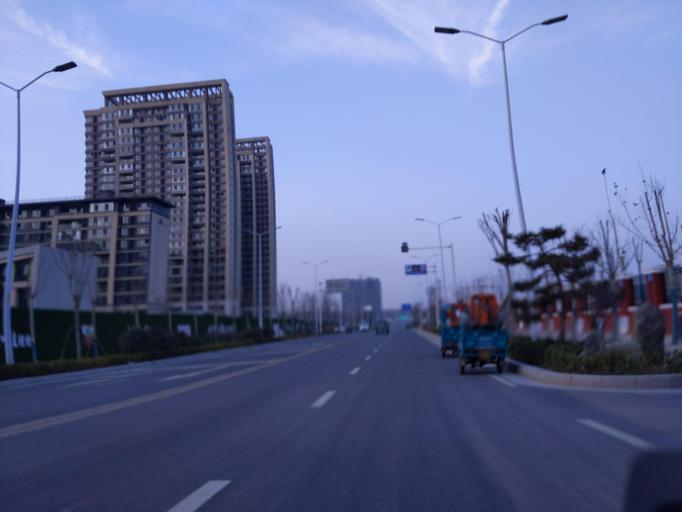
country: CN
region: Henan Sheng
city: Puyang
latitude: 35.8073
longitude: 115.0113
